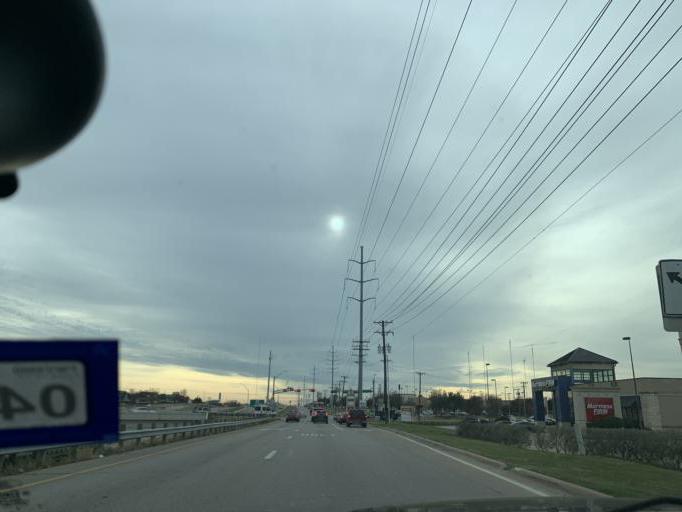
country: US
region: Texas
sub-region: Dallas County
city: Cedar Hill
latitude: 32.6053
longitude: -96.9311
